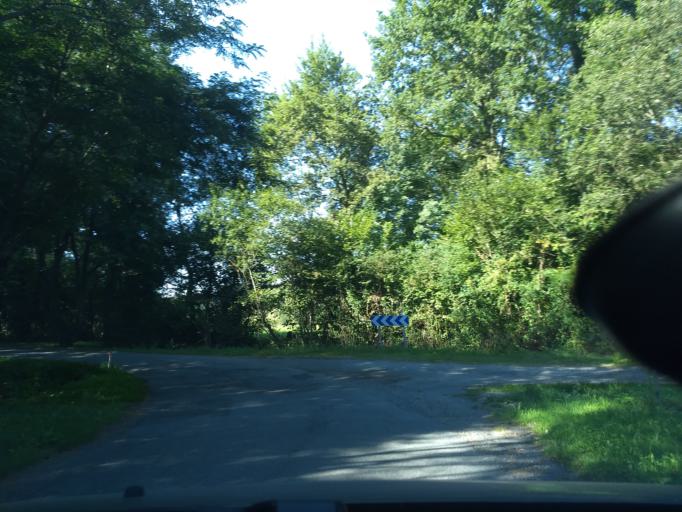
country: FR
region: Aquitaine
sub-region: Departement des Pyrenees-Atlantiques
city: Soumoulou
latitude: 43.2906
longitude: -0.1464
